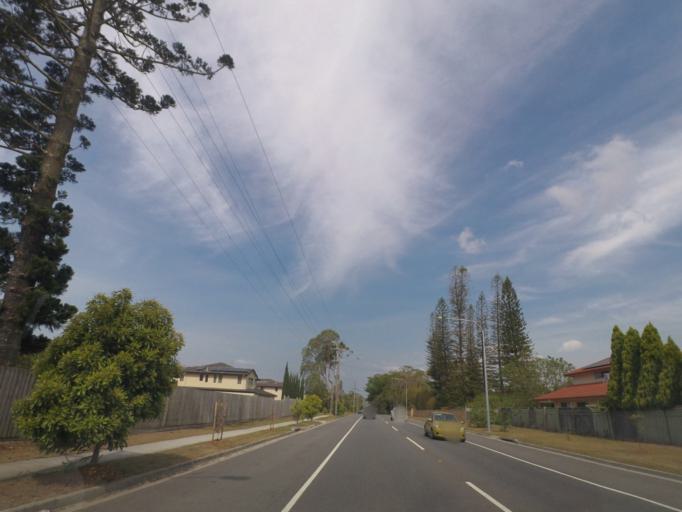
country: AU
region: Queensland
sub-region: Brisbane
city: Sunnybank
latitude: -27.5976
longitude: 153.0459
